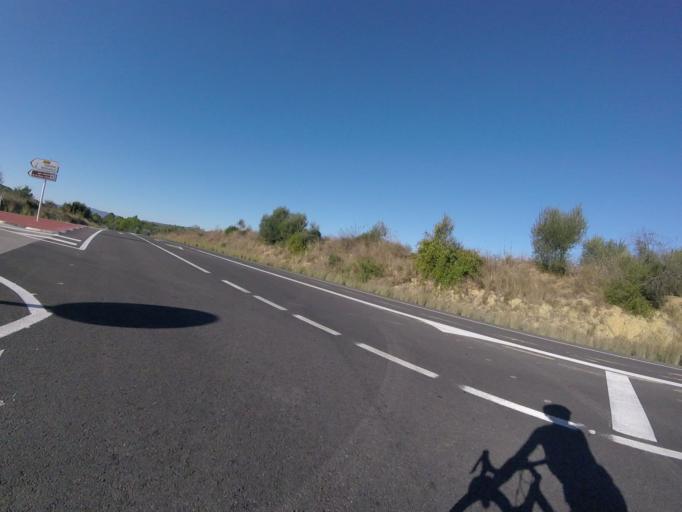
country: ES
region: Valencia
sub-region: Provincia de Castello
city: Cervera del Maestre
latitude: 40.4776
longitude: 0.2168
